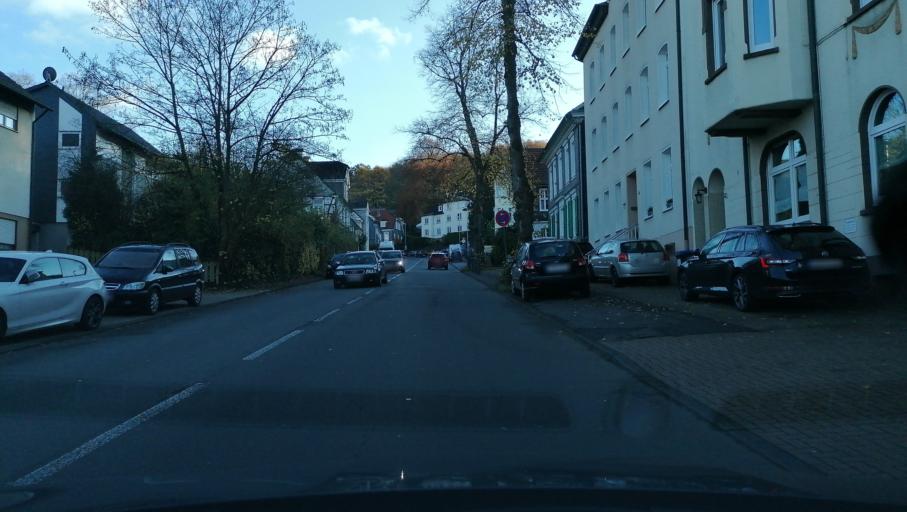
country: DE
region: North Rhine-Westphalia
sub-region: Regierungsbezirk Arnsberg
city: Schwelm
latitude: 51.2805
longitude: 7.2940
